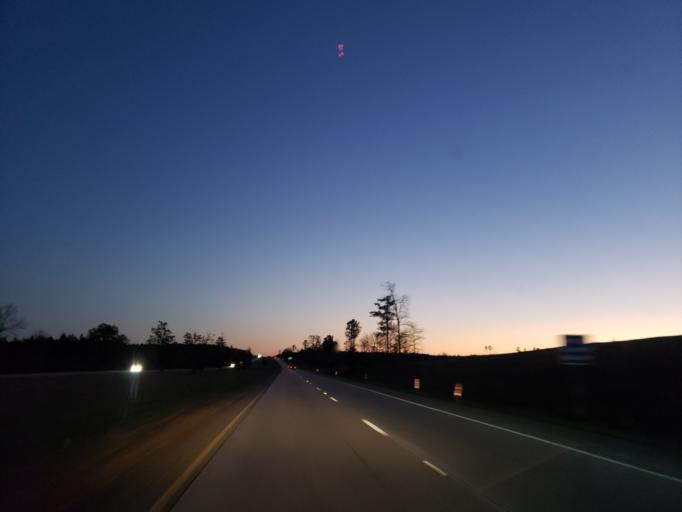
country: US
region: Mississippi
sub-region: Forrest County
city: Rawls Springs
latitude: 31.4550
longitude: -89.3221
